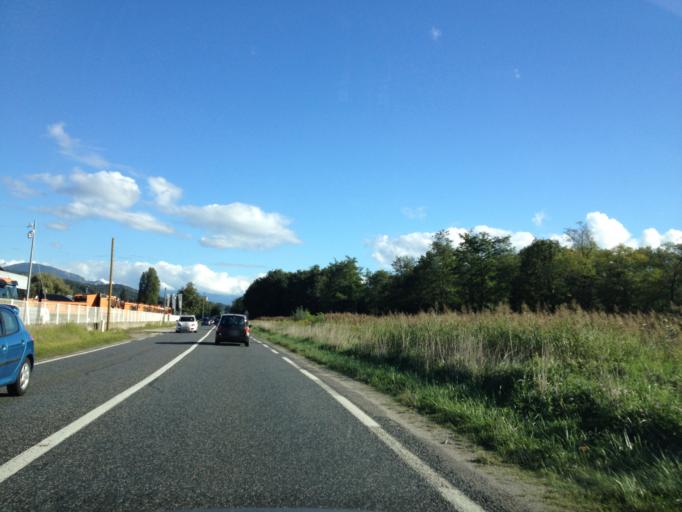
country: FR
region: Rhone-Alpes
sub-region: Departement de la Savoie
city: Voglans
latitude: 45.6228
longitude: 5.8770
